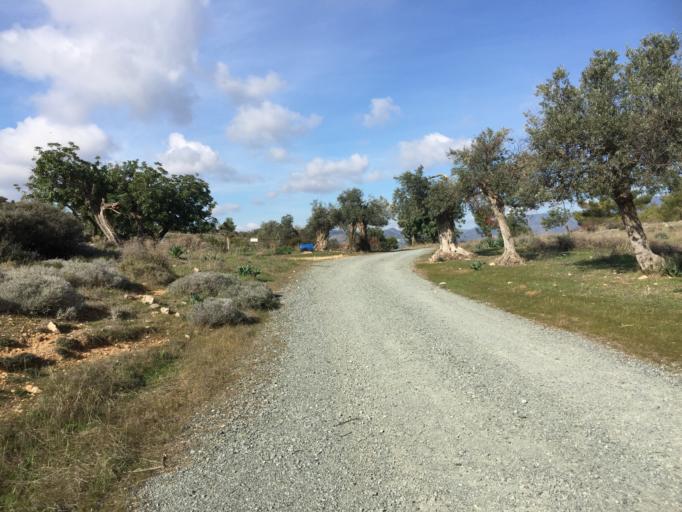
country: CY
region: Larnaka
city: Agios Tychon
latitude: 34.7473
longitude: 33.1263
